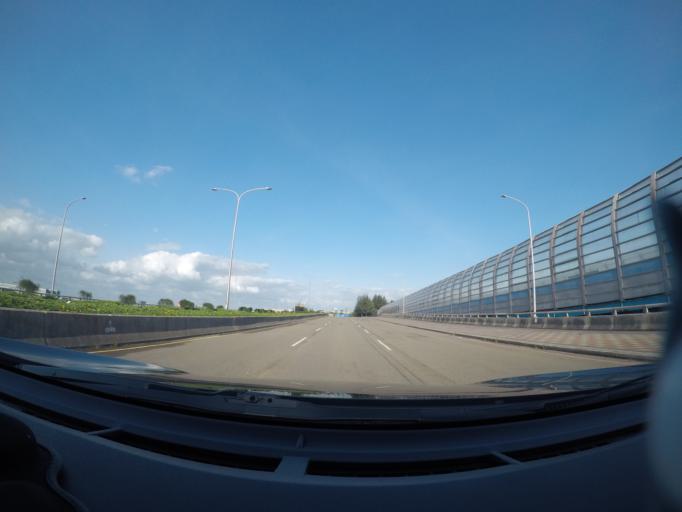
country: TW
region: Taiwan
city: Taoyuan City
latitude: 25.0984
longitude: 121.2506
